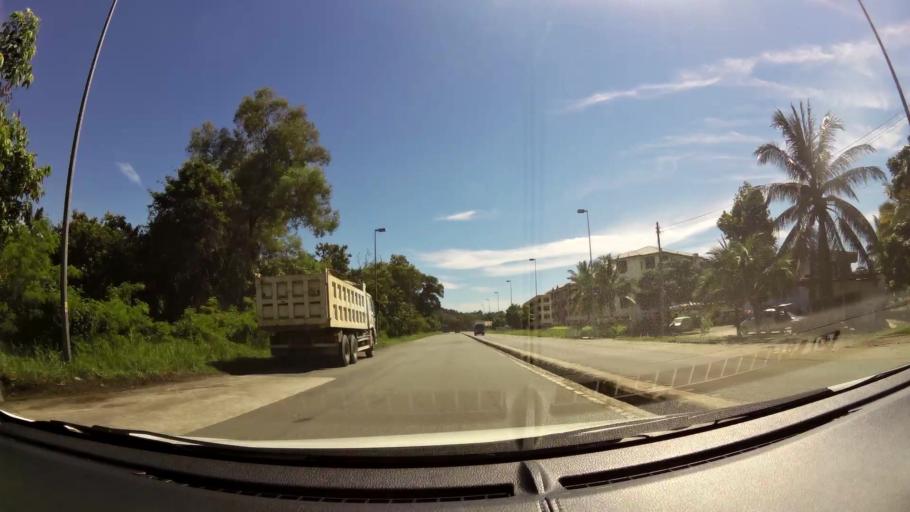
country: BN
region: Brunei and Muara
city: Bandar Seri Begawan
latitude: 5.0242
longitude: 115.0647
